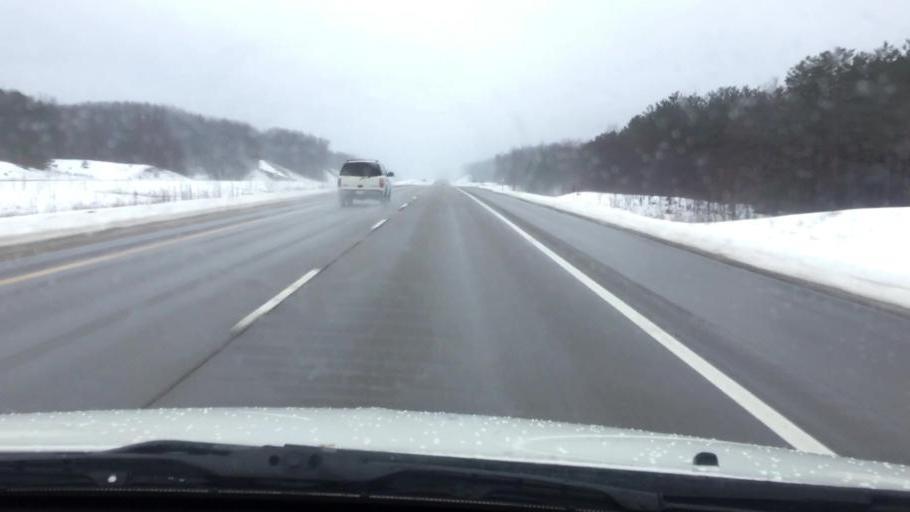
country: US
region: Michigan
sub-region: Wexford County
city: Manton
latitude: 44.3629
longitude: -85.4028
